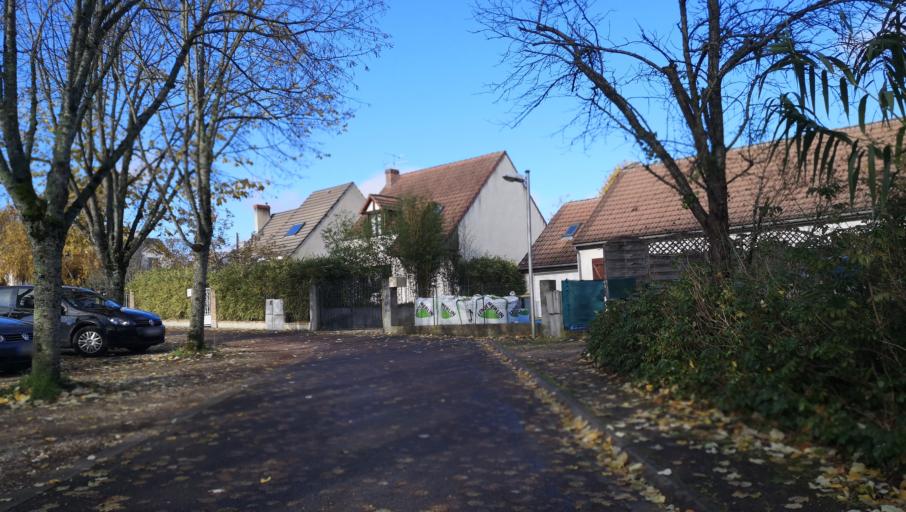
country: FR
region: Centre
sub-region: Departement du Loiret
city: Semoy
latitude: 47.9068
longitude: 1.9416
